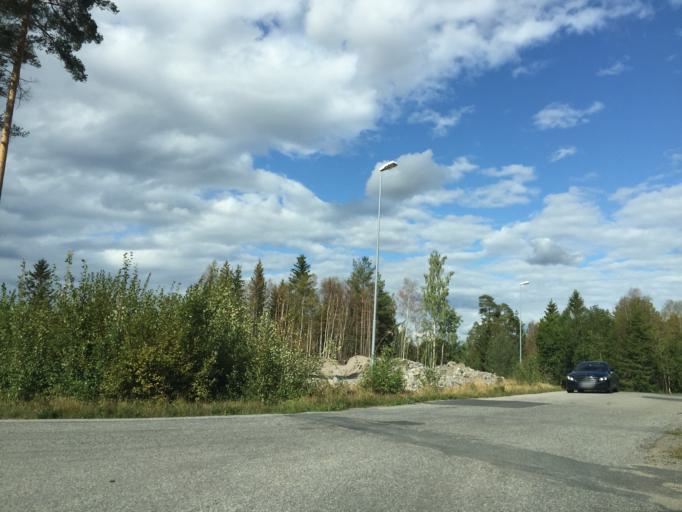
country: NO
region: Ostfold
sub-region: Askim
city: Askim
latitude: 59.5929
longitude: 11.1294
